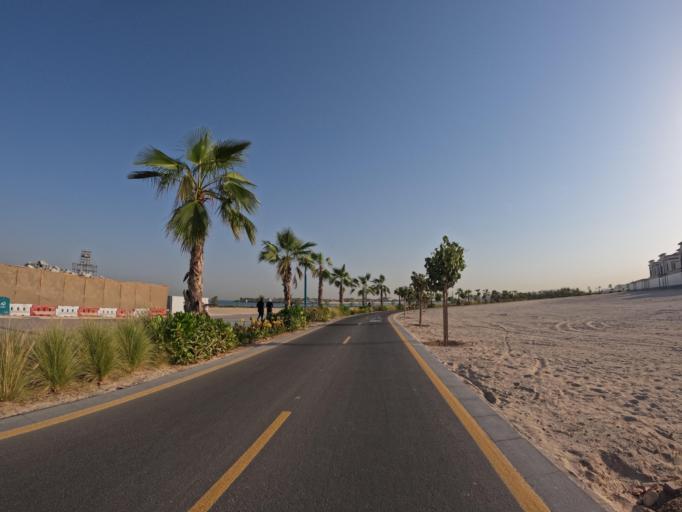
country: AE
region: Dubai
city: Dubai
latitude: 25.1908
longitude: 55.2279
